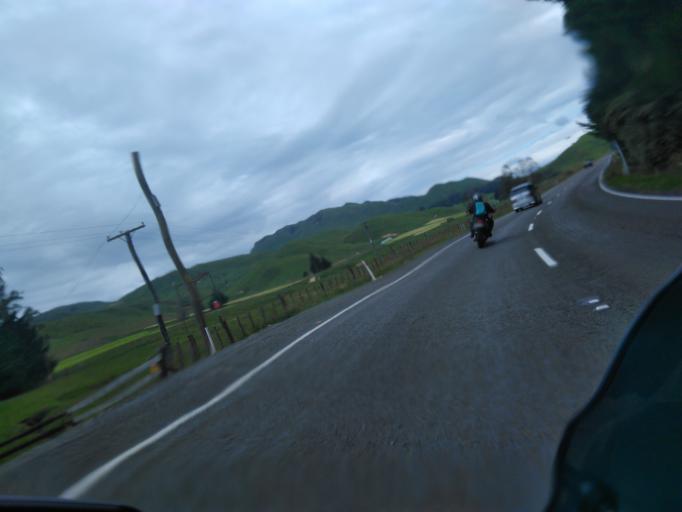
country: NZ
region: Bay of Plenty
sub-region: Opotiki District
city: Opotiki
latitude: -38.3590
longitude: 177.5406
